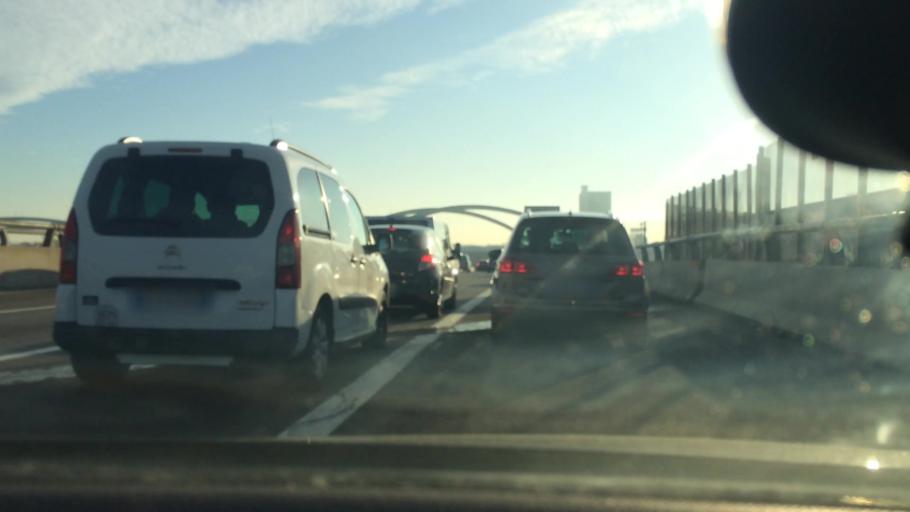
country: IT
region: Lombardy
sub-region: Citta metropolitana di Milano
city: Baranzate
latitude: 45.5148
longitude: 9.1070
